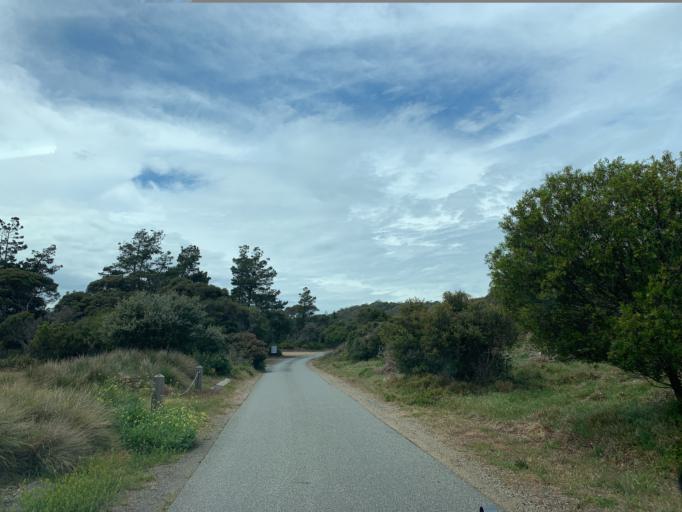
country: AU
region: Victoria
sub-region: Queenscliffe
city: Queenscliff
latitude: -38.3142
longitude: 144.6885
